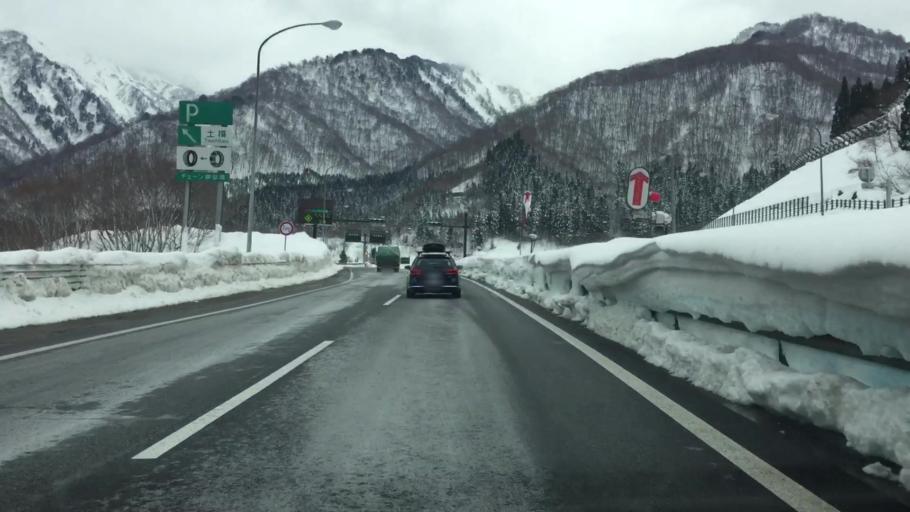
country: JP
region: Niigata
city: Shiozawa
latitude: 36.8670
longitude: 138.8707
